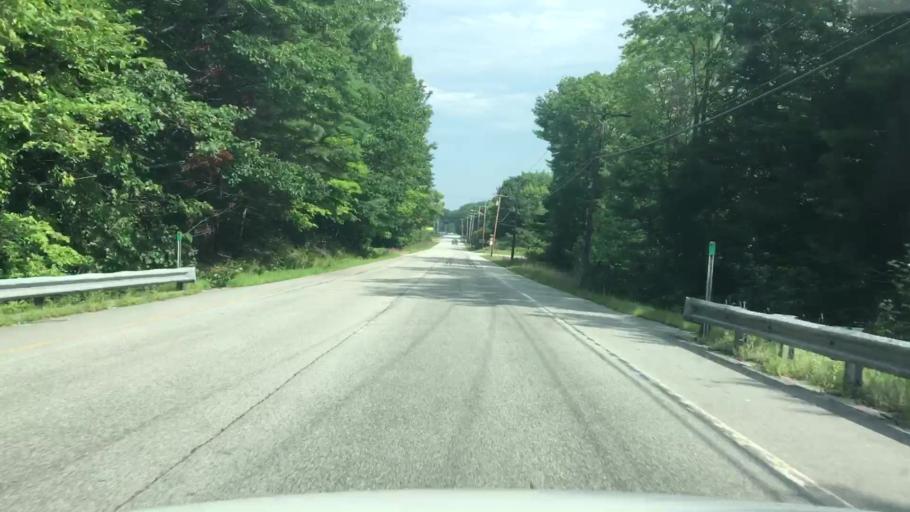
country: US
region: Maine
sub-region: Androscoggin County
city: Auburn
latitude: 44.0541
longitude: -70.2533
